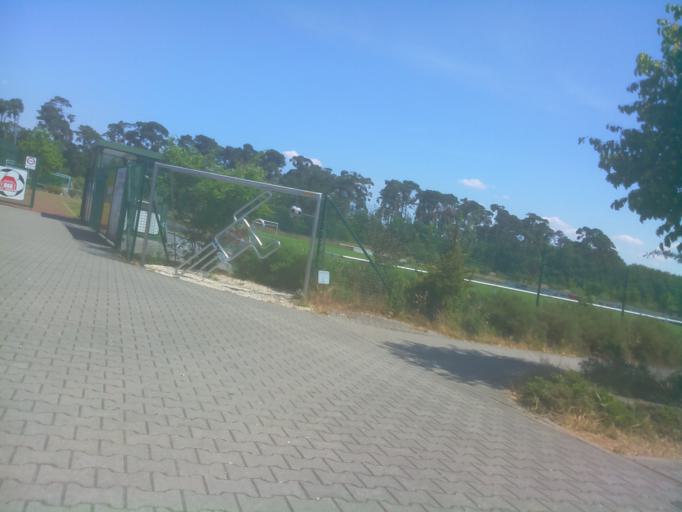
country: DE
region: Hesse
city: Lorsch
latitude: 49.6368
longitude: 8.5739
